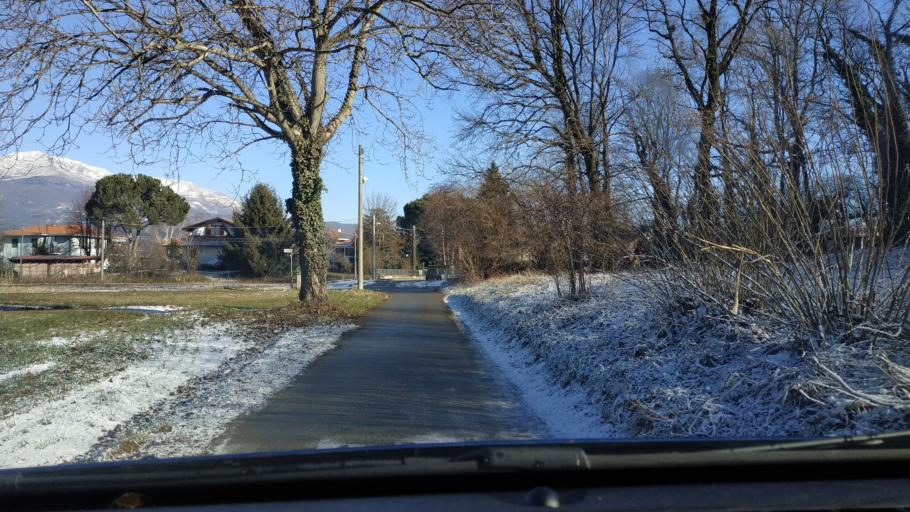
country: IT
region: Piedmont
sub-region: Provincia di Torino
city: Salerano Canavese
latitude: 45.4599
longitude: 7.8474
